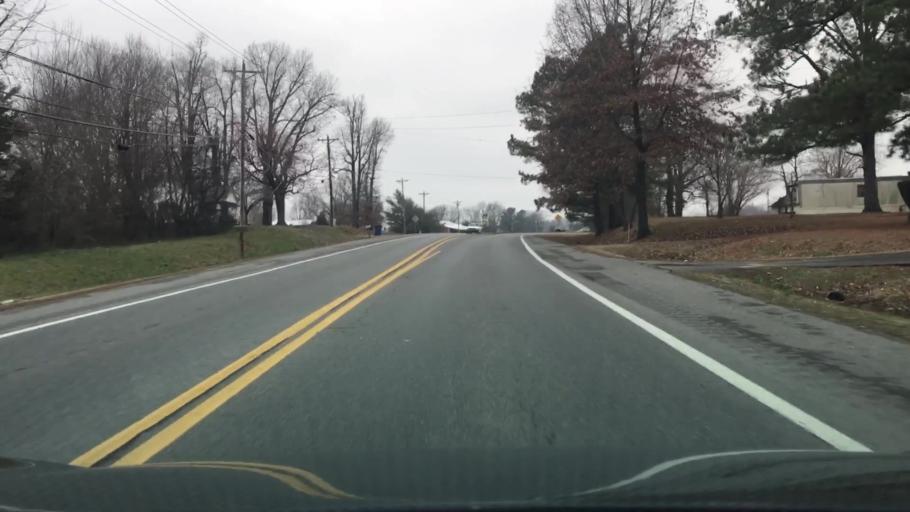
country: US
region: Kentucky
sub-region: McCracken County
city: Reidland
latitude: 36.9874
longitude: -88.5020
